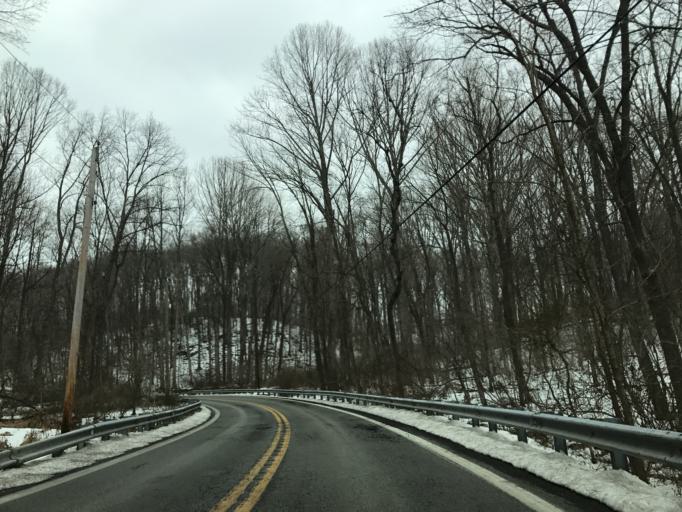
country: US
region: Maryland
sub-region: Harford County
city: Jarrettsville
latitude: 39.6464
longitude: -76.4104
